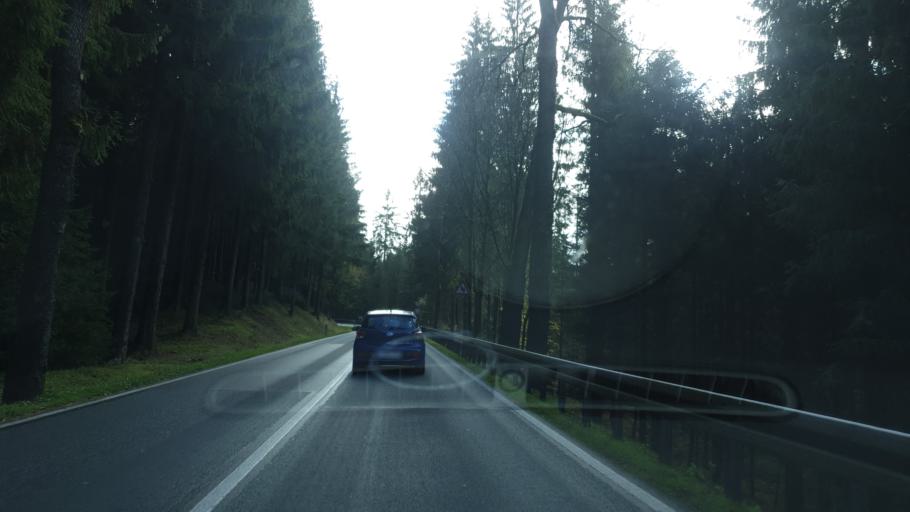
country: DE
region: Saxony
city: Eibenstock
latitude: 50.5127
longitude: 12.6081
